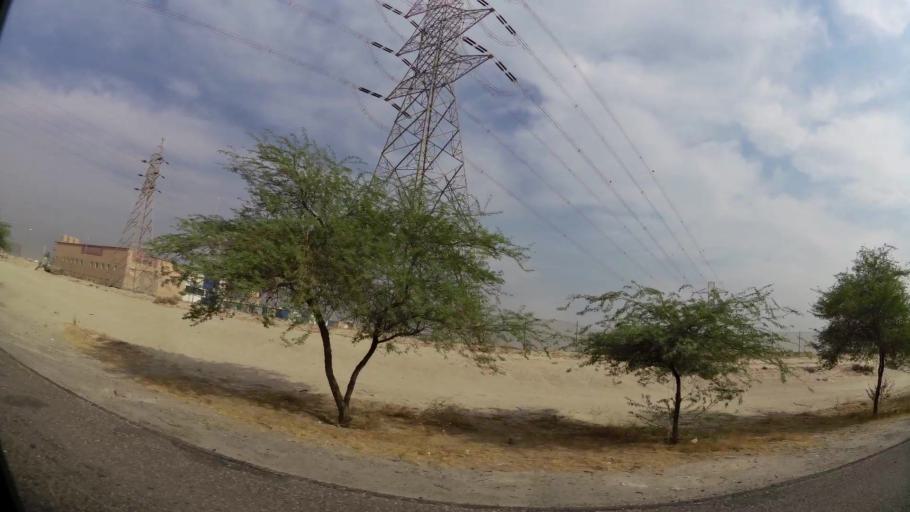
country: KW
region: Muhafazat al Jahra'
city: Al Jahra'
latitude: 29.2934
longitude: 47.7486
